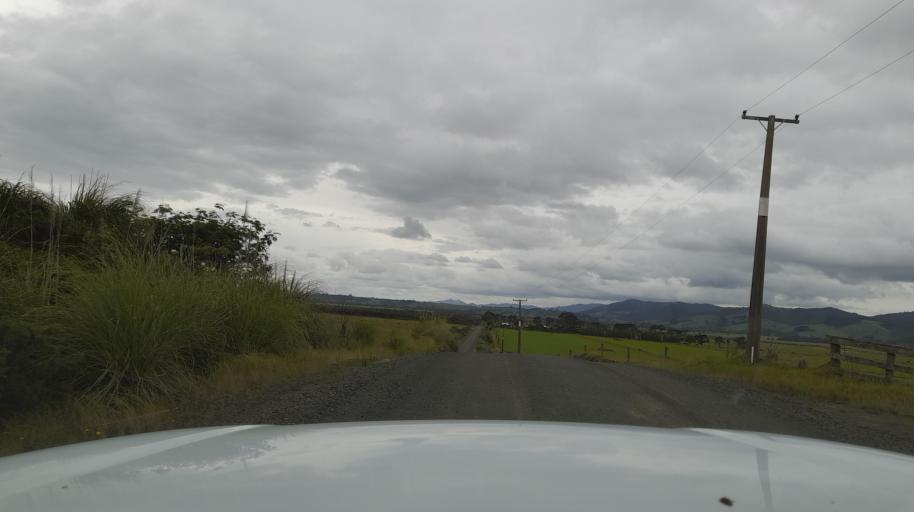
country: NZ
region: Northland
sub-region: Far North District
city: Ahipara
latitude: -35.1330
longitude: 173.1858
